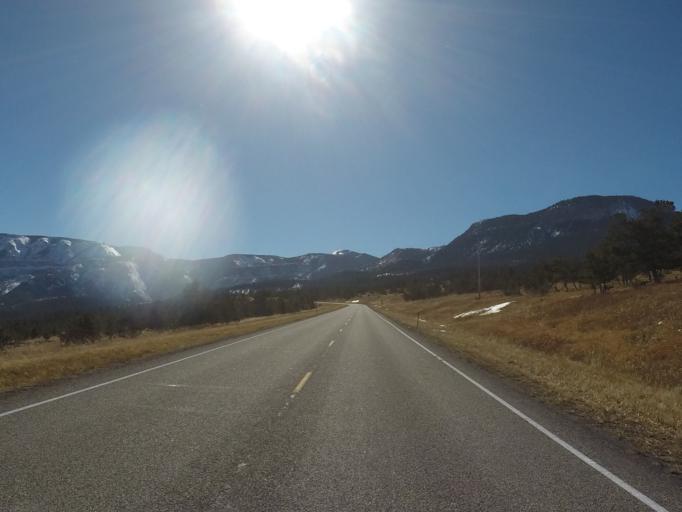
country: US
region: Wyoming
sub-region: Park County
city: Cody
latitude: 44.7180
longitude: -109.3240
